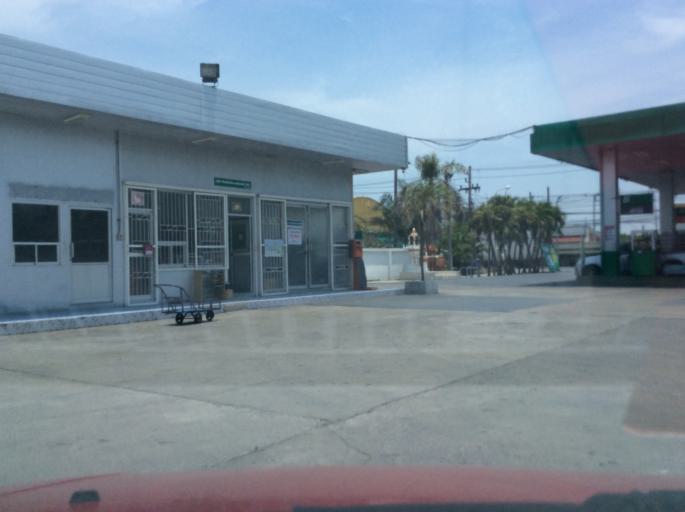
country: TH
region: Pathum Thani
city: Lam Luk Ka
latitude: 13.9629
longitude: 100.7471
